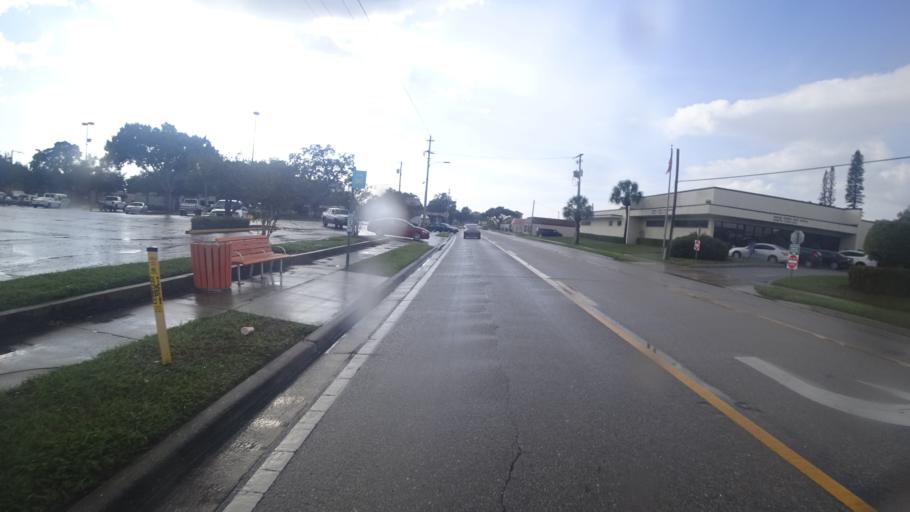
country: US
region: Florida
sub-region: Manatee County
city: Palmetto
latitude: 27.5175
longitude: -82.5702
